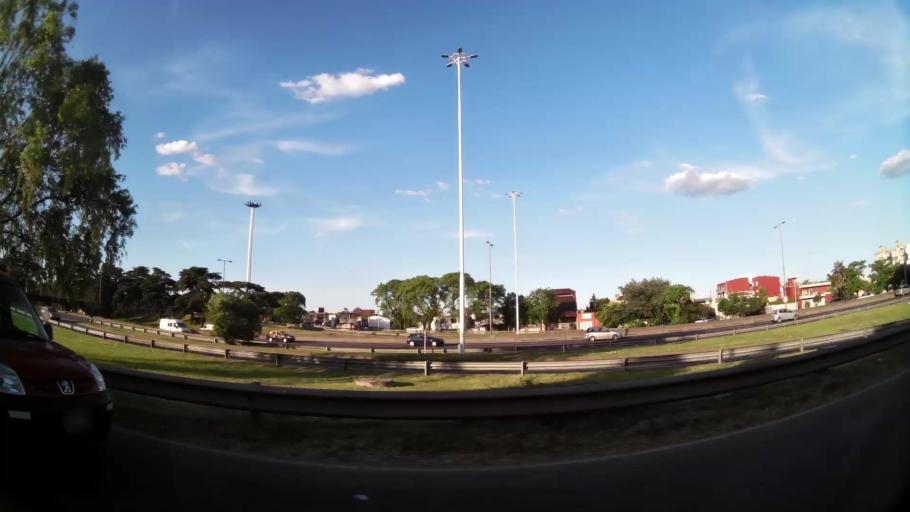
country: AR
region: Buenos Aires F.D.
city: Villa Lugano
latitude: -34.6894
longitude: -58.4828
